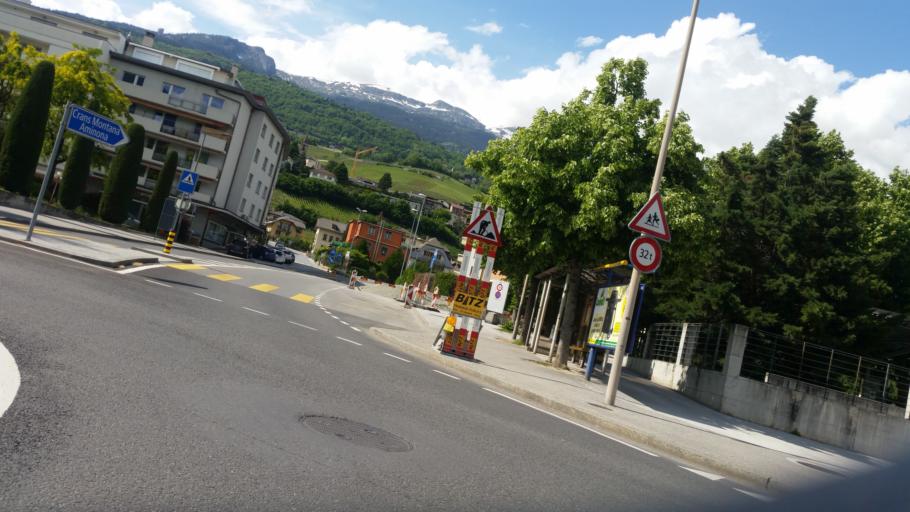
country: CH
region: Valais
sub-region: Sierre District
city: Sierre
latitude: 46.2941
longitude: 7.5335
